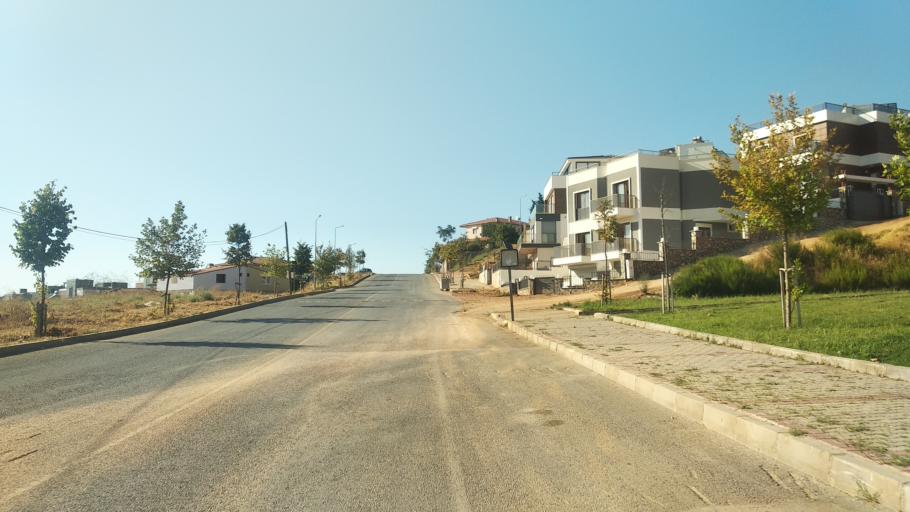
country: TR
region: Izmir
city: Urla
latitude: 38.3584
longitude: 26.8808
